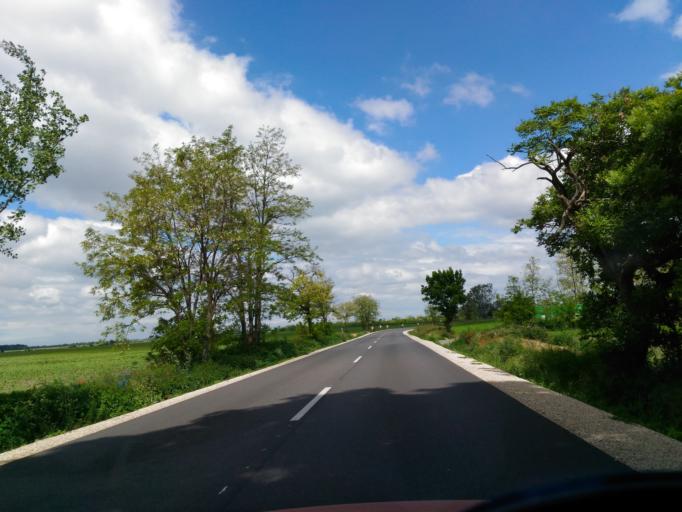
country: HU
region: Fejer
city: Pusztaszabolcs
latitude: 47.1643
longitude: 18.7299
